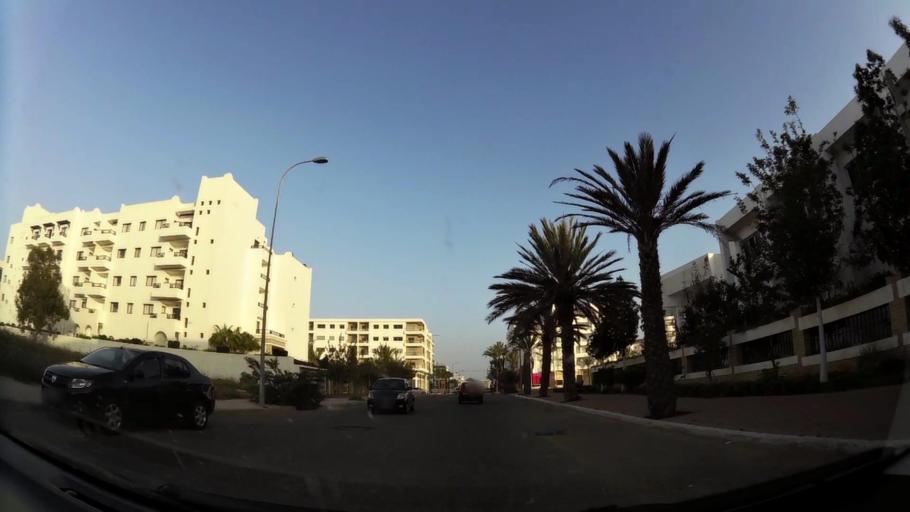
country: MA
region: Souss-Massa-Draa
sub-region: Agadir-Ida-ou-Tnan
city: Agadir
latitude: 30.4017
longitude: -9.5922
